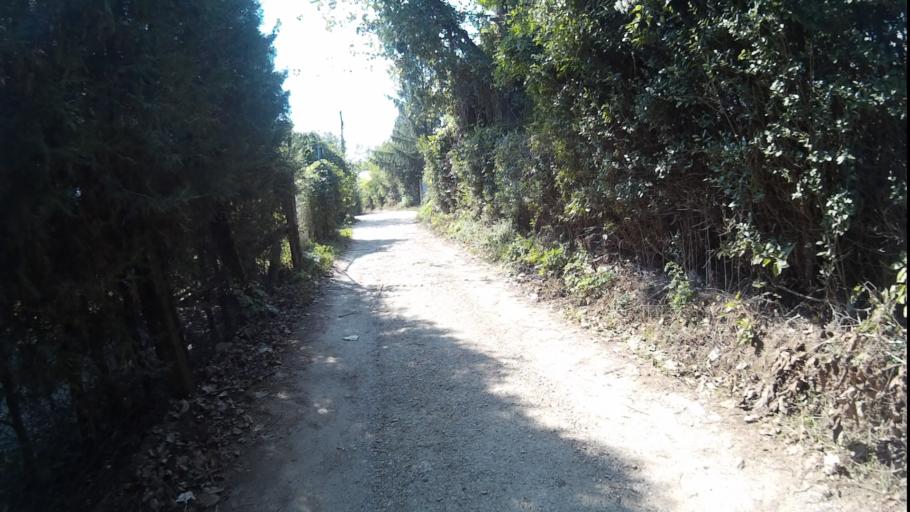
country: RS
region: Central Serbia
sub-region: Nisavski Okrug
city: Nis
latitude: 43.3024
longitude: 21.9126
